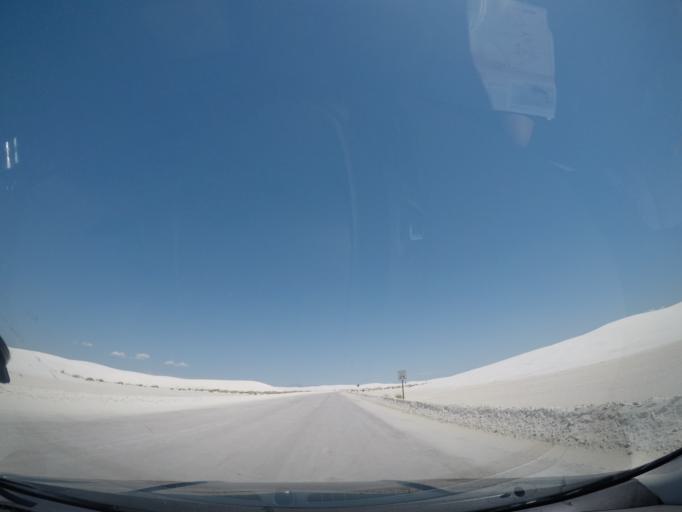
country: US
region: New Mexico
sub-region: Otero County
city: Holloman Air Force Base
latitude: 32.8135
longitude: -106.2637
